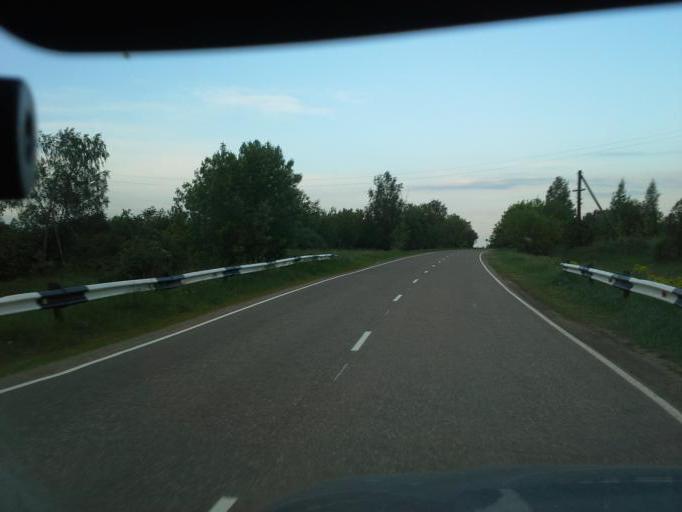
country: RU
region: Ivanovo
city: Gavrilov Posad
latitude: 56.5486
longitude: 40.1791
